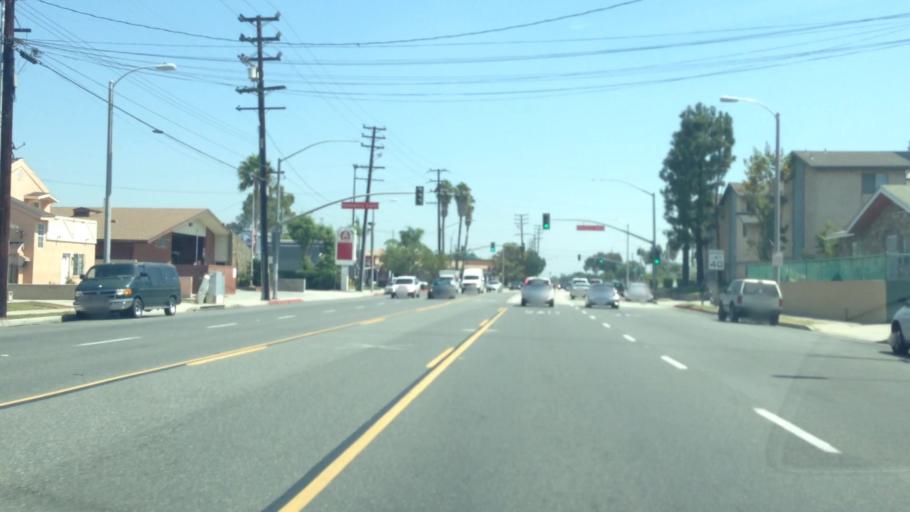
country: US
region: California
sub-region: Los Angeles County
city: Carson
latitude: 33.8243
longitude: -118.2779
